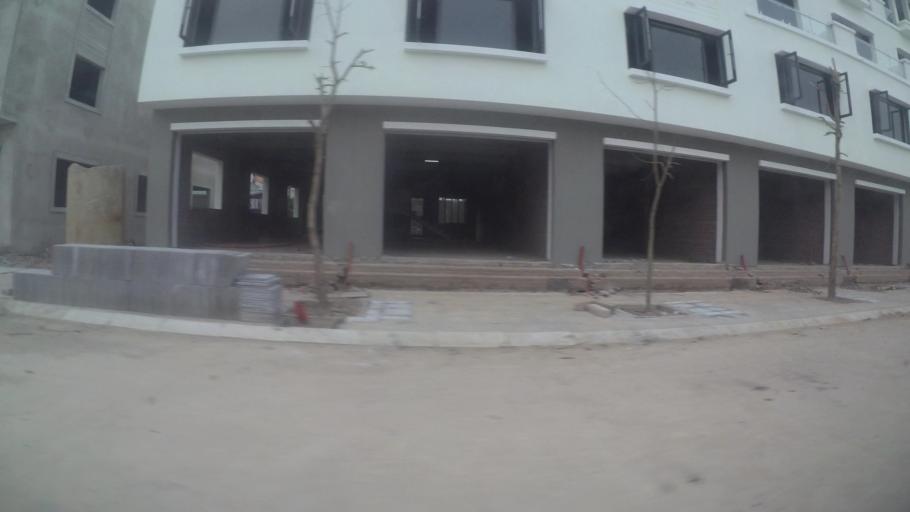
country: VN
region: Ha Noi
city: Ha Dong
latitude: 20.9959
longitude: 105.7337
